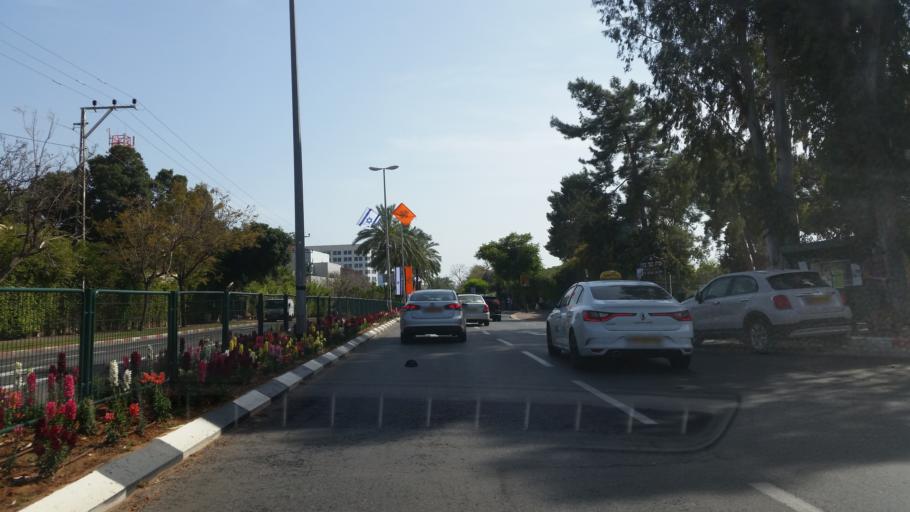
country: IL
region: Central District
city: Ra'anana
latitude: 32.1895
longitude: 34.8550
